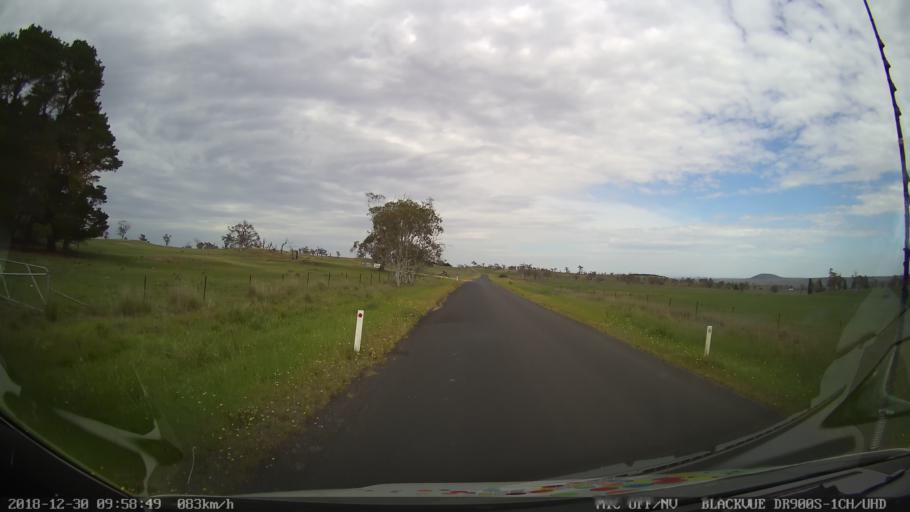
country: AU
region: New South Wales
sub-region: Cooma-Monaro
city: Cooma
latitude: -36.5224
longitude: 149.2204
